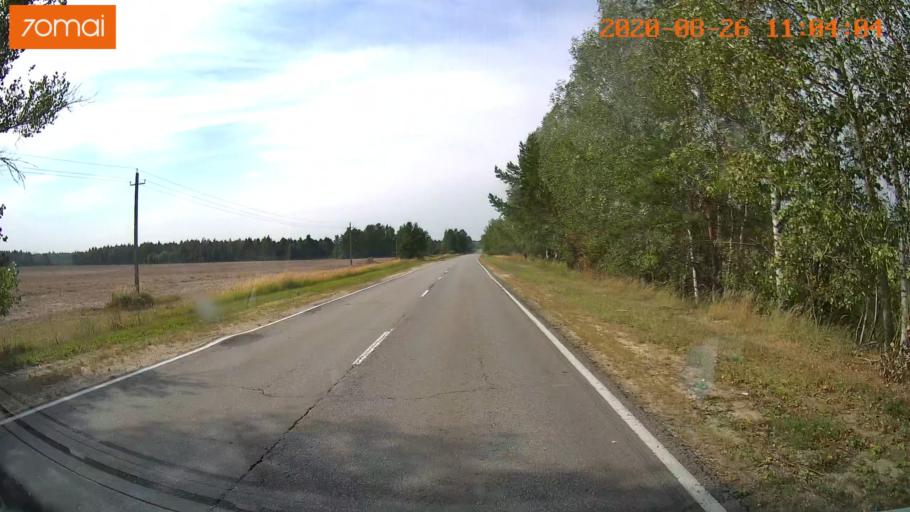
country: RU
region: Rjazan
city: Izhevskoye
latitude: 54.5340
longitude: 41.2018
